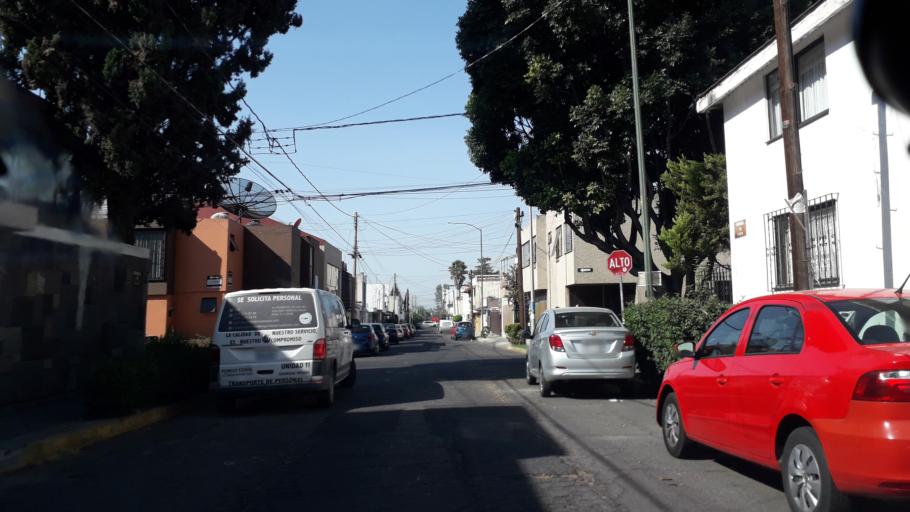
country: MX
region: Puebla
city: Puebla
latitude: 19.0287
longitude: -98.2151
